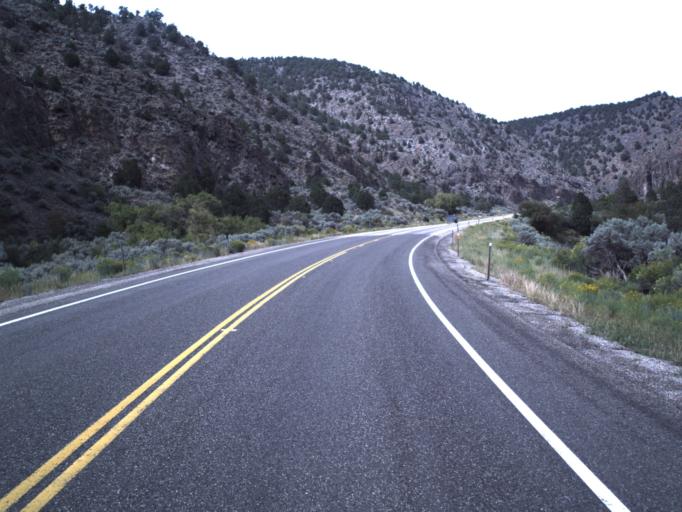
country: US
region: Utah
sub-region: Piute County
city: Junction
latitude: 38.1106
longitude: -112.3375
